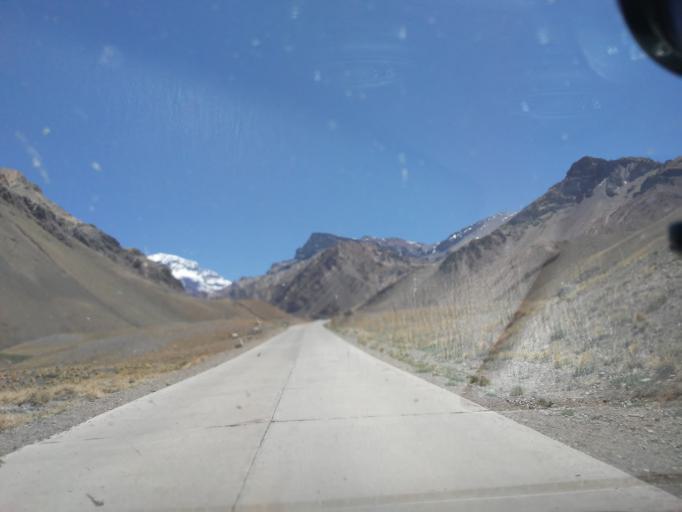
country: CL
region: Valparaiso
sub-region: Provincia de Los Andes
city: Los Andes
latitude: -32.8211
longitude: -69.9421
